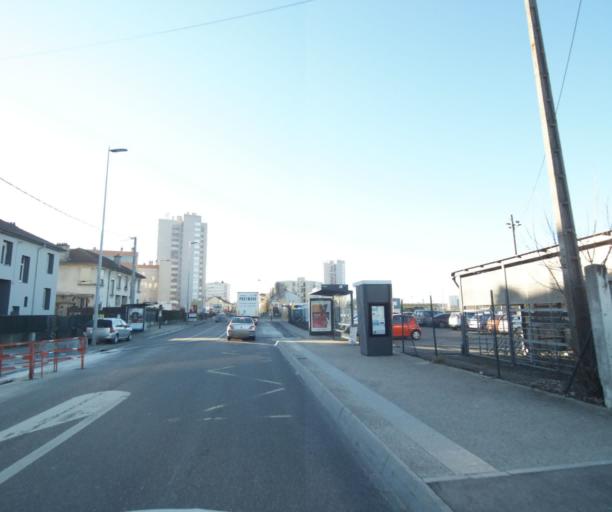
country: FR
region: Lorraine
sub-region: Departement de Meurthe-et-Moselle
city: Jarville-la-Malgrange
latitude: 48.6664
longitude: 6.2139
